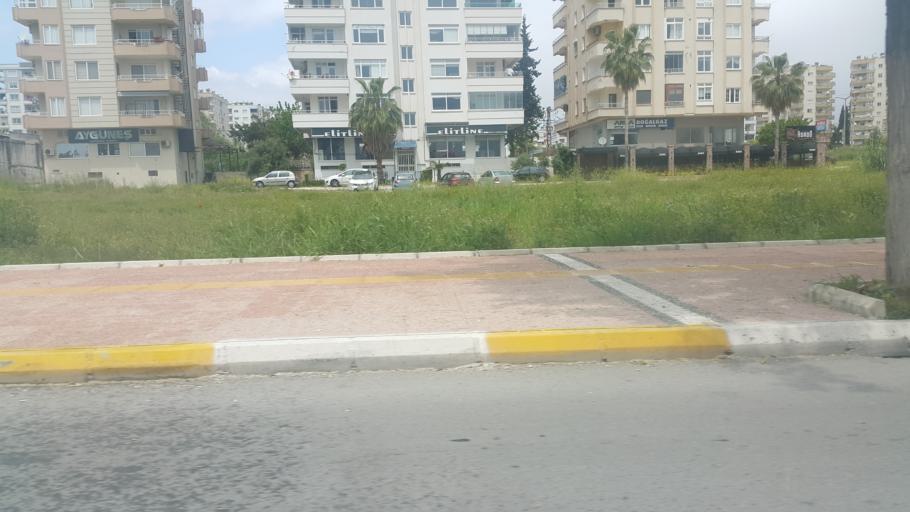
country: TR
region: Mersin
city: Mercin
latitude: 36.7679
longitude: 34.5600
